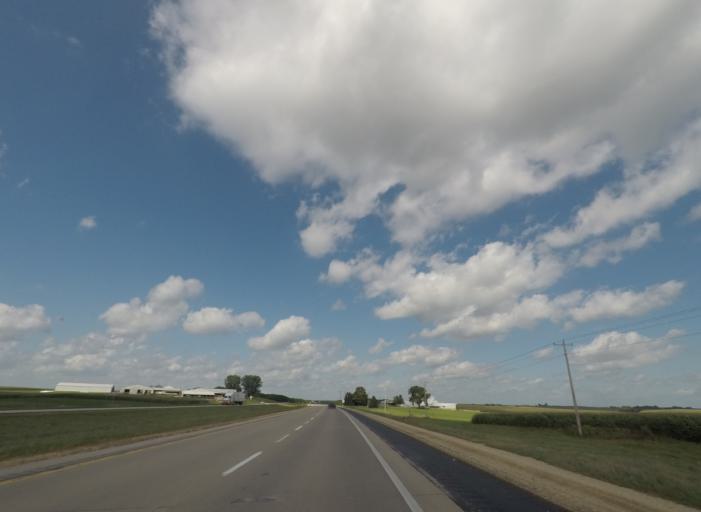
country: US
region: Iowa
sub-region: Jones County
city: Monticello
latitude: 42.2686
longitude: -91.1429
